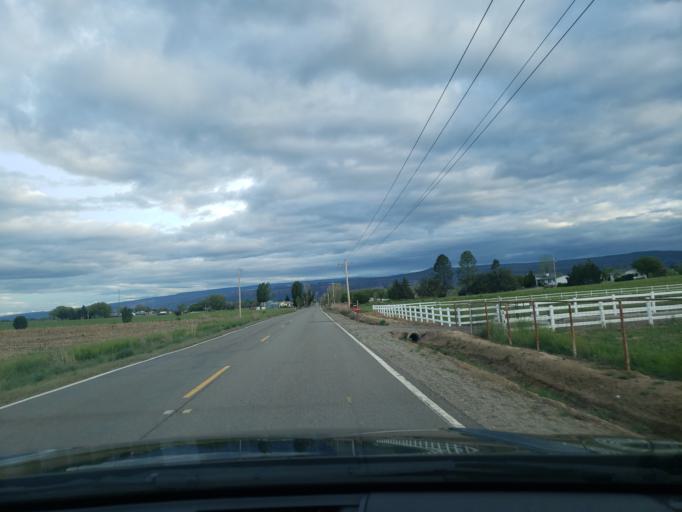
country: US
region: Colorado
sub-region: Mesa County
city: Fruita
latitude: 39.2129
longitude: -108.7011
